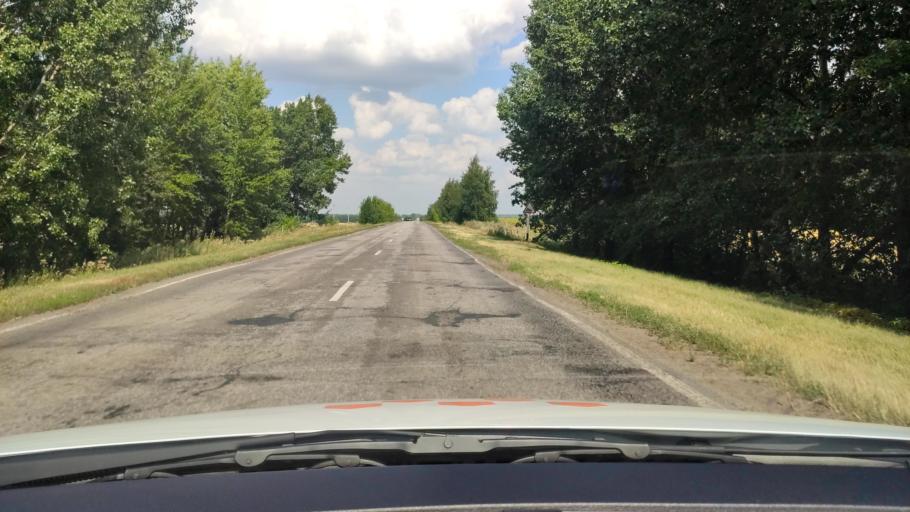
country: RU
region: Voronezj
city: Pereleshinskiy
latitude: 51.7353
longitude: 40.3877
